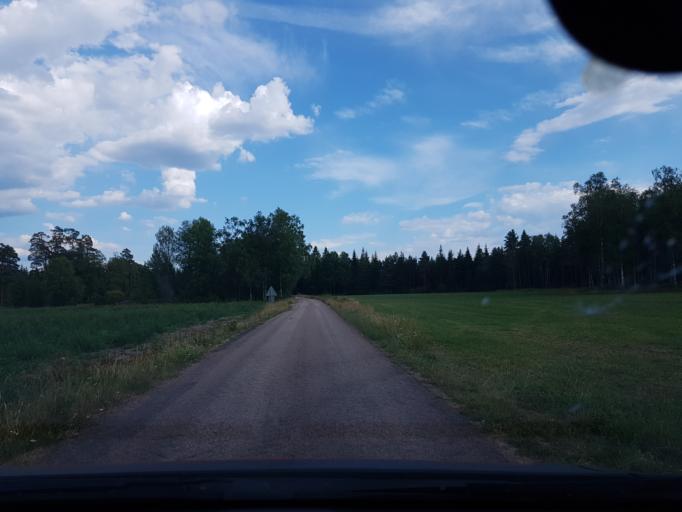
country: SE
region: Joenkoeping
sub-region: Gislaveds Kommun
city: Reftele
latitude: 57.2123
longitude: 13.5806
